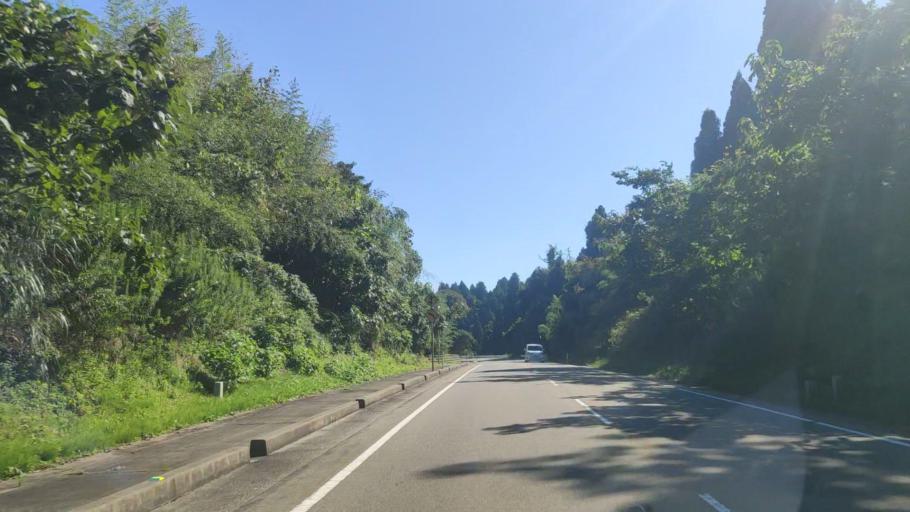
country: JP
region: Ishikawa
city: Nanao
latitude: 37.3793
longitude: 137.2337
